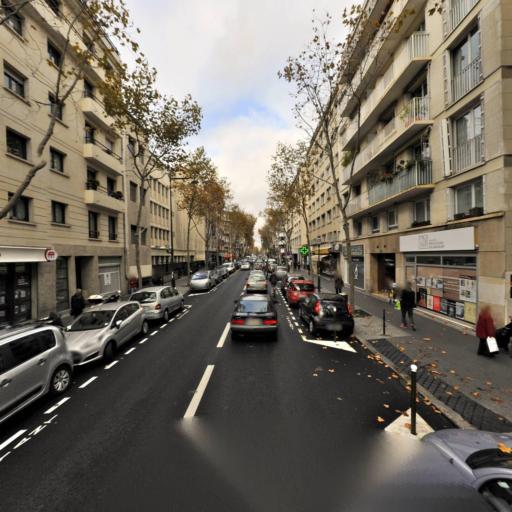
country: FR
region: Ile-de-France
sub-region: Departement des Hauts-de-Seine
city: Boulogne-Billancourt
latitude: 48.8316
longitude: 2.2447
